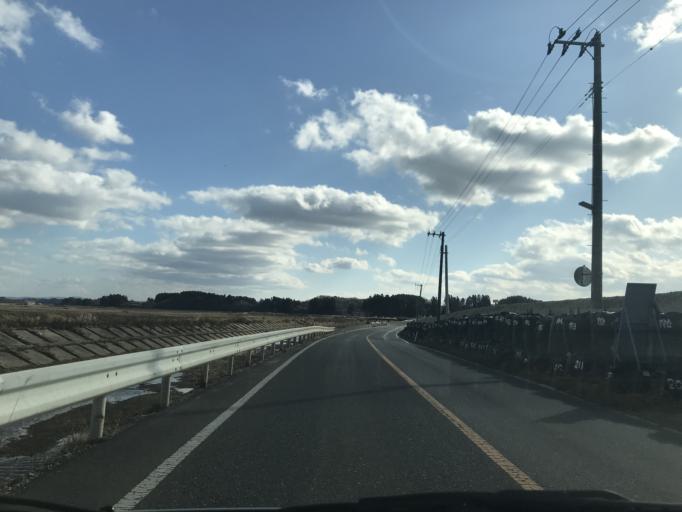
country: JP
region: Miyagi
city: Kogota
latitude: 38.7258
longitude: 141.0623
